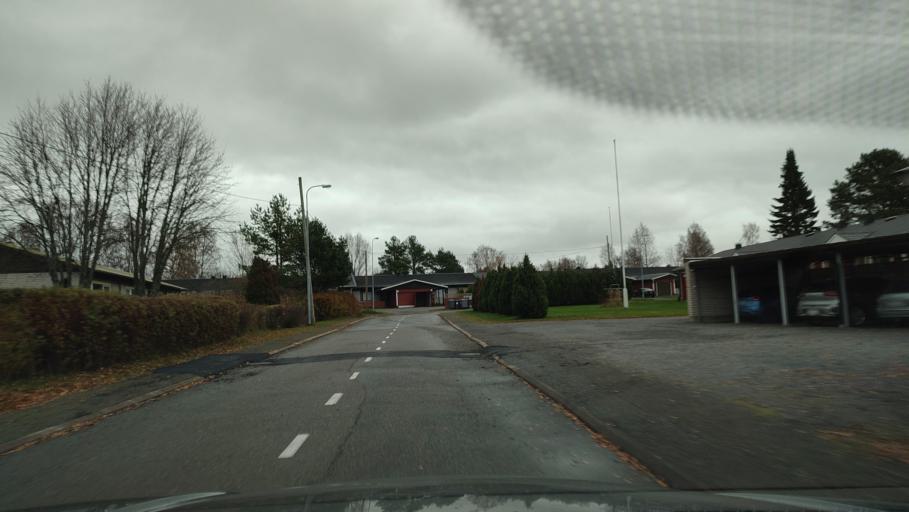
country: FI
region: Ostrobothnia
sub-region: Sydosterbotten
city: Kristinestad
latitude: 62.2807
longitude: 21.3662
